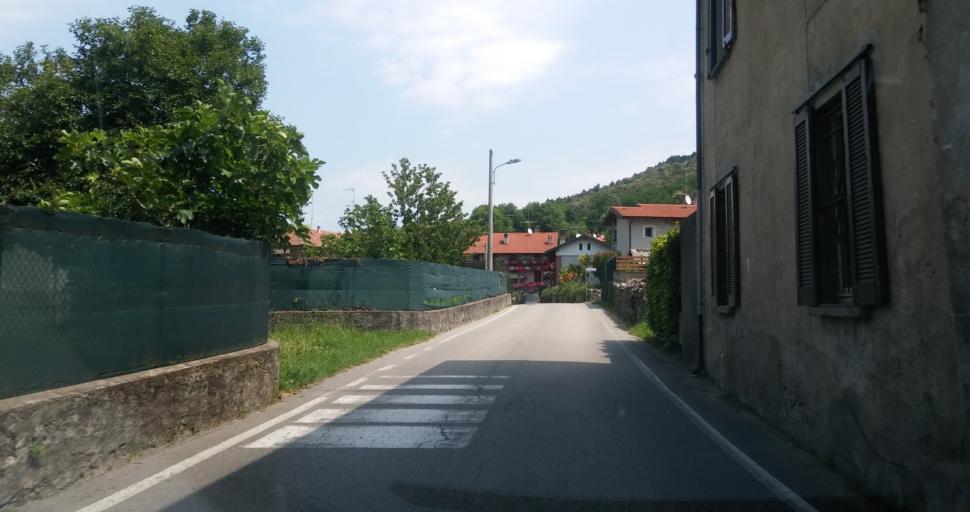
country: IT
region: Lombardy
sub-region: Provincia di Varese
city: Osmate
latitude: 45.7682
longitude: 8.6532
